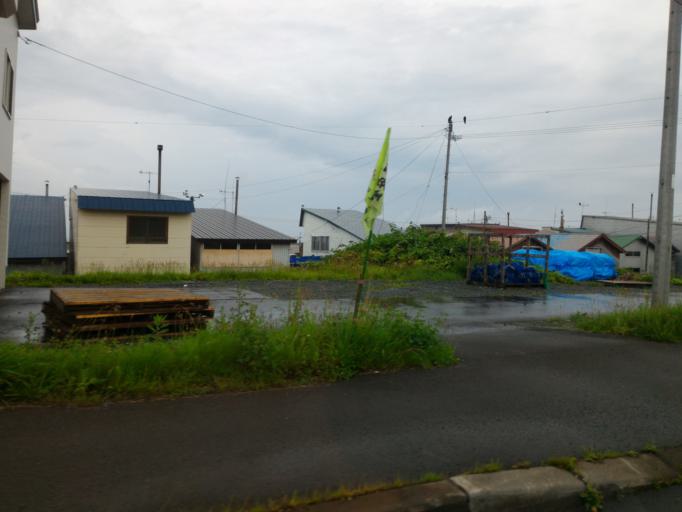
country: JP
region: Hokkaido
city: Rumoi
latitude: 43.9961
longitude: 141.6522
